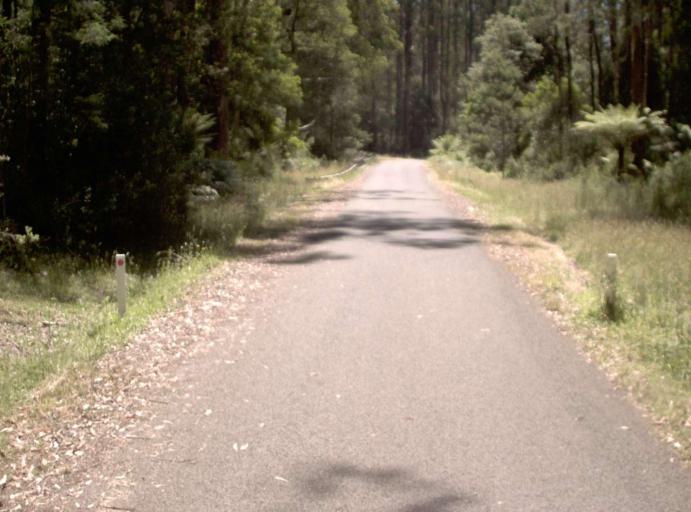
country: AU
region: Victoria
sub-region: Yarra Ranges
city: Millgrove
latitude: -37.6470
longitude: 145.7255
